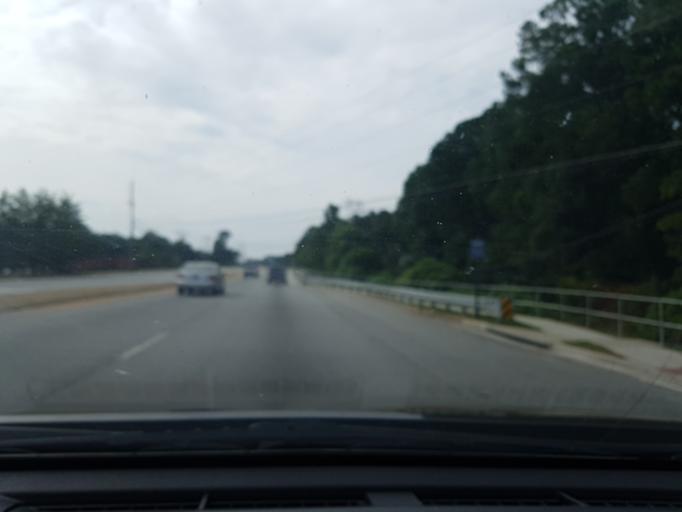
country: US
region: Georgia
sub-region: Gwinnett County
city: Norcross
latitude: 33.9364
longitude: -84.1851
